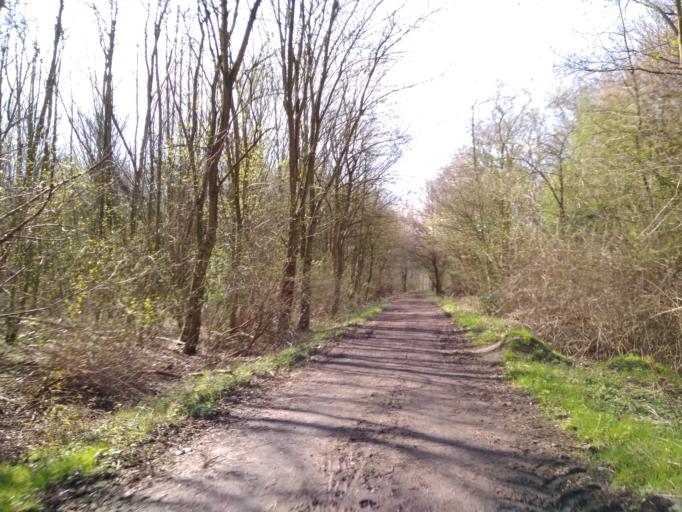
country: DE
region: North Rhine-Westphalia
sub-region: Regierungsbezirk Munster
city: Gladbeck
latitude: 51.6042
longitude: 7.0002
